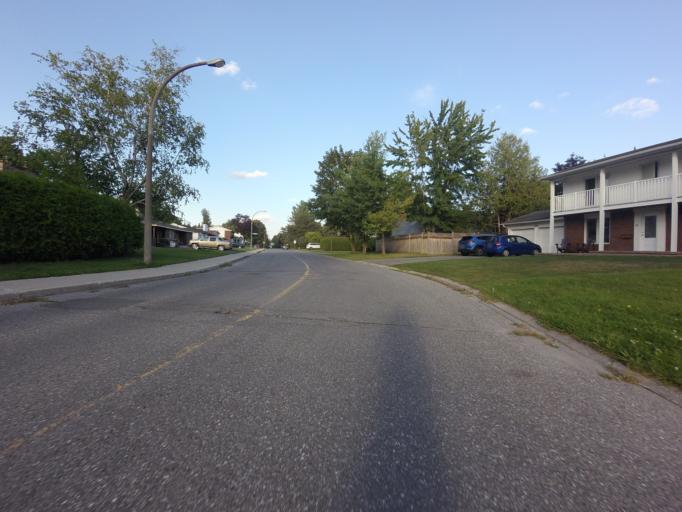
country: CA
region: Ontario
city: Bells Corners
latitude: 45.3359
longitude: -75.7781
